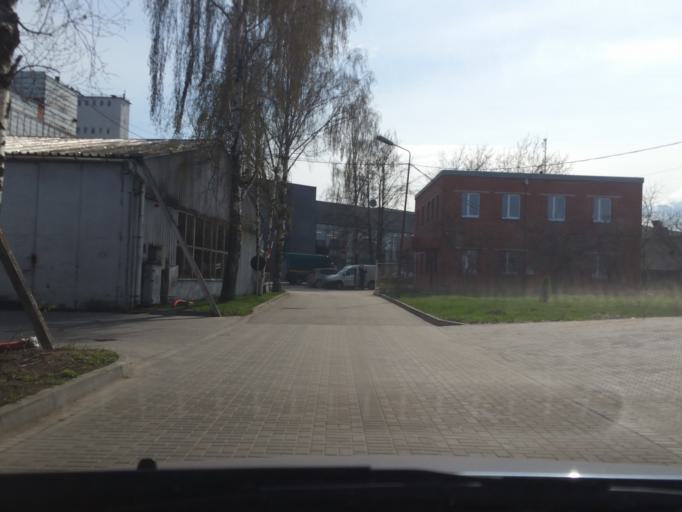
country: LV
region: Riga
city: Jaunciems
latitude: 56.9897
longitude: 24.1961
